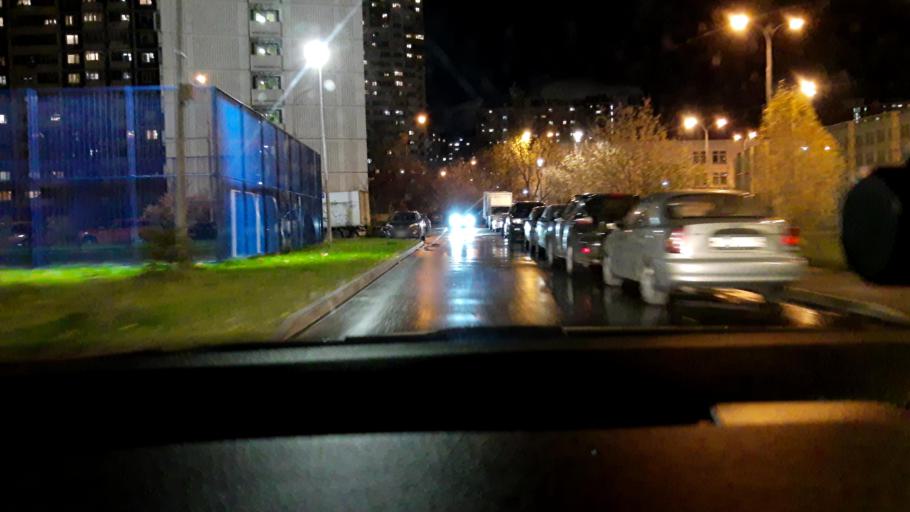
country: RU
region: Moscow
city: Lyublino
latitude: 55.6654
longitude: 37.7568
